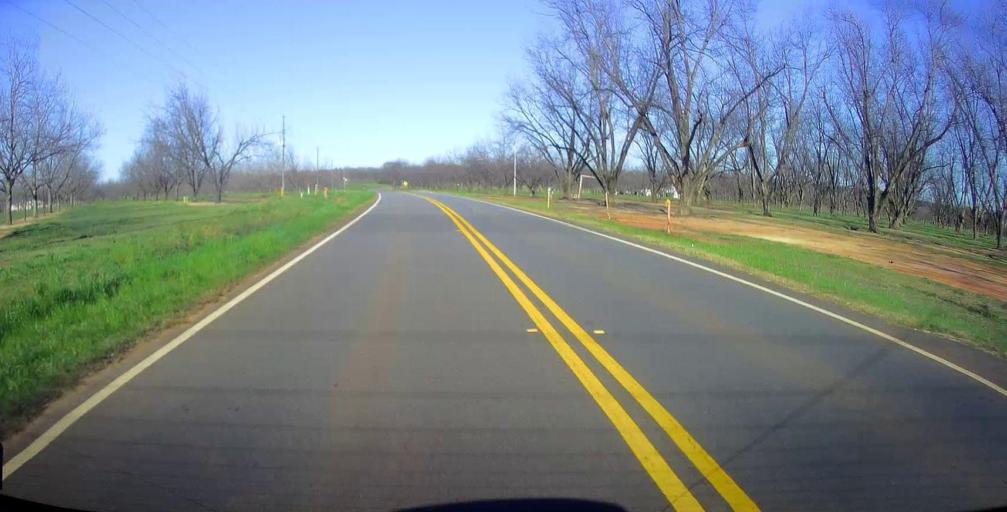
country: US
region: Georgia
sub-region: Peach County
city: Byron
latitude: 32.6769
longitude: -83.8538
